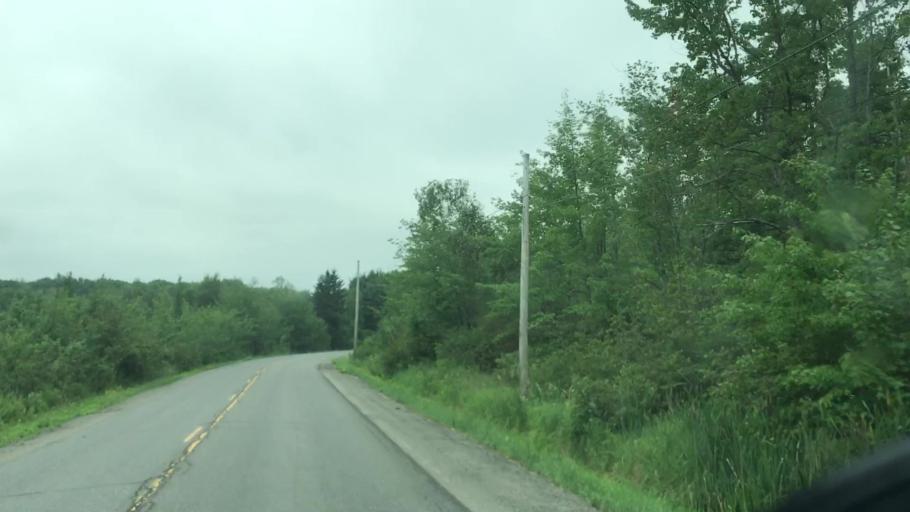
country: US
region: Maine
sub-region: Penobscot County
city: Veazie
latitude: 44.8681
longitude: -68.7163
